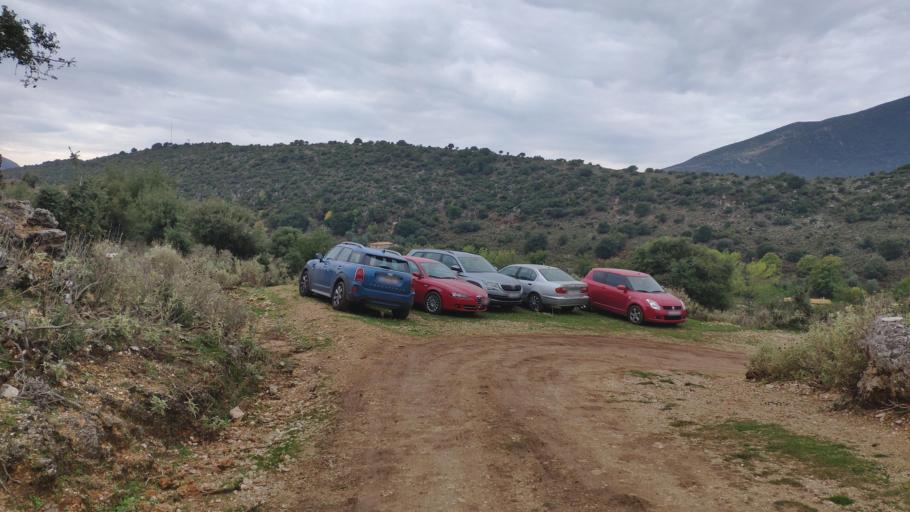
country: GR
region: Epirus
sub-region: Nomos Prevezis
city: Kanalaki
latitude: 39.3622
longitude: 20.6438
